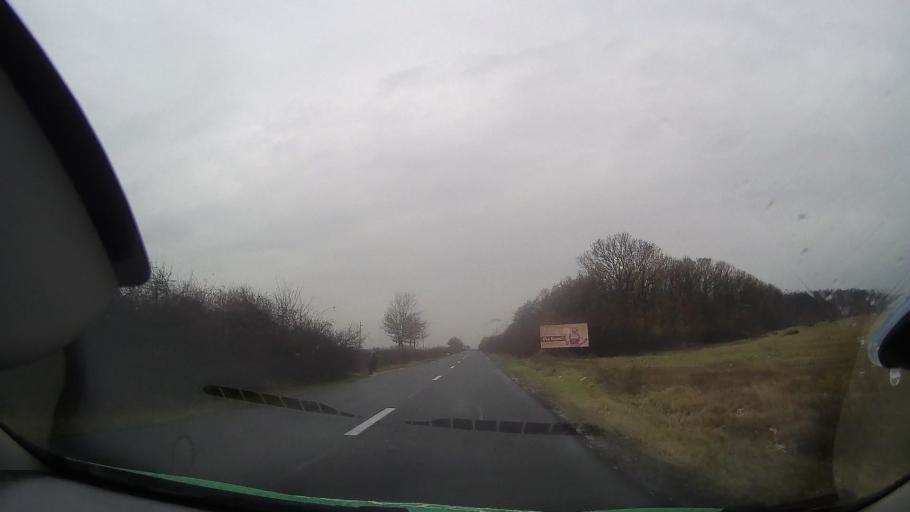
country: RO
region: Bihor
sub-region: Comuna Tinca
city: Gurbediu
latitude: 46.7738
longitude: 21.8876
